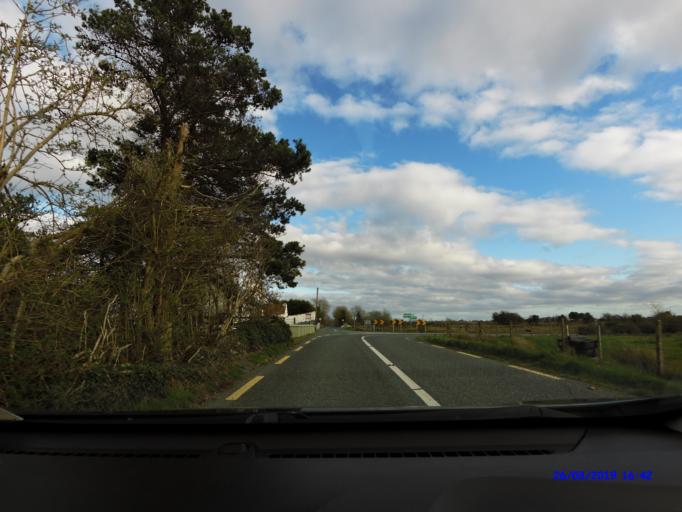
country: IE
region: Connaught
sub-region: Maigh Eo
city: Ballyhaunis
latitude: 53.8659
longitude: -8.7637
